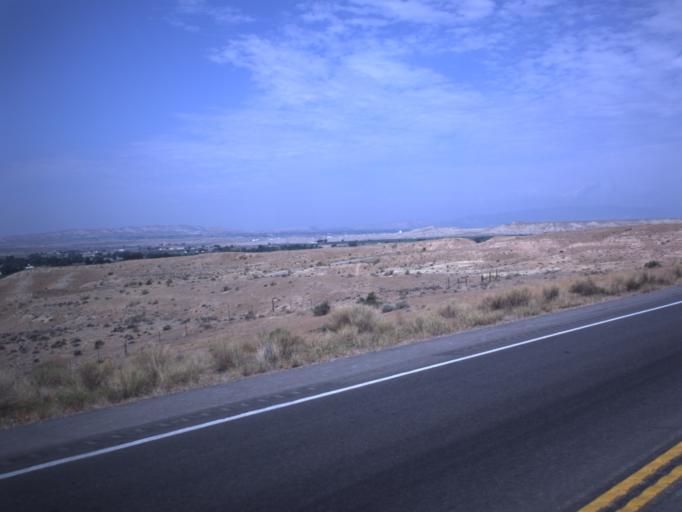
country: US
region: Utah
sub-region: Uintah County
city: Naples
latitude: 40.3647
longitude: -109.3218
